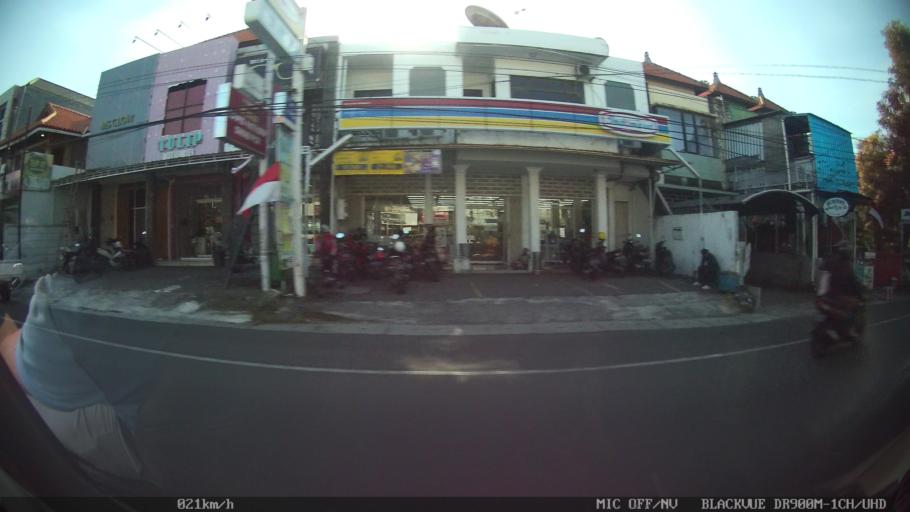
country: ID
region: Bali
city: Jimbaran
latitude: -8.7872
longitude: 115.1875
